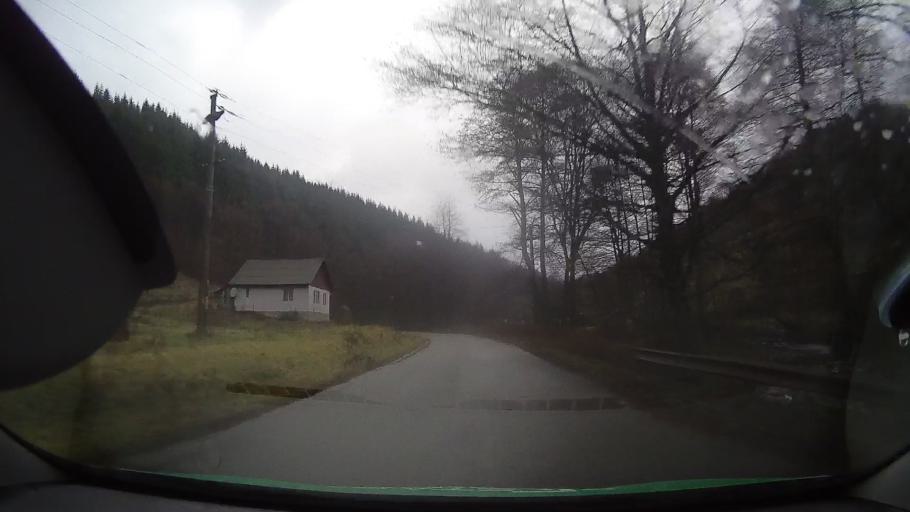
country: RO
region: Alba
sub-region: Comuna Avram Iancu
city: Avram Iancu
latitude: 46.2923
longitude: 22.7540
